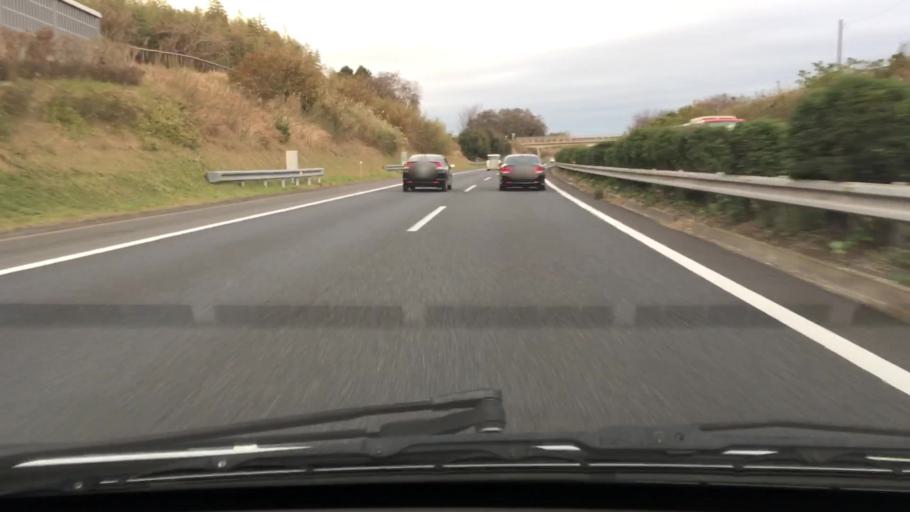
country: JP
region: Chiba
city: Kisarazu
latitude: 35.4244
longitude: 140.0216
